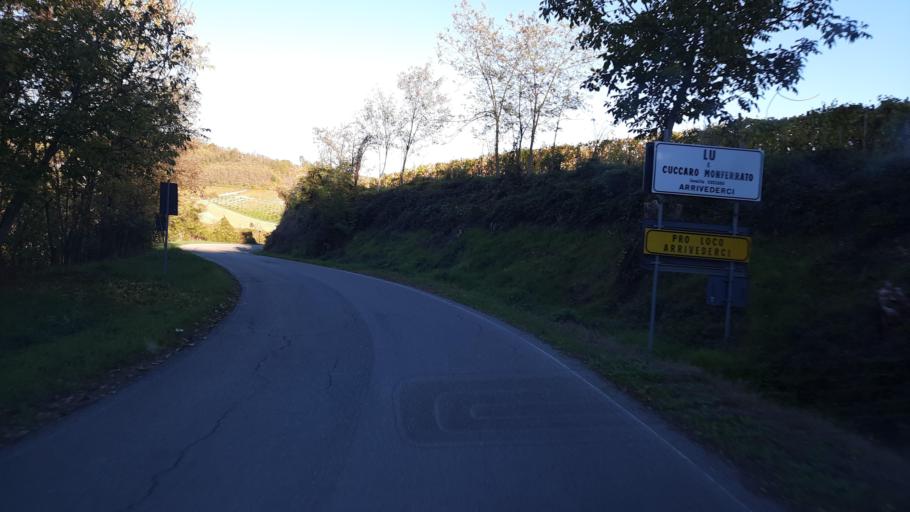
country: IT
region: Piedmont
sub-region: Provincia di Alessandria
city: Cuccaro Monferrato
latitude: 44.9913
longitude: 8.4607
